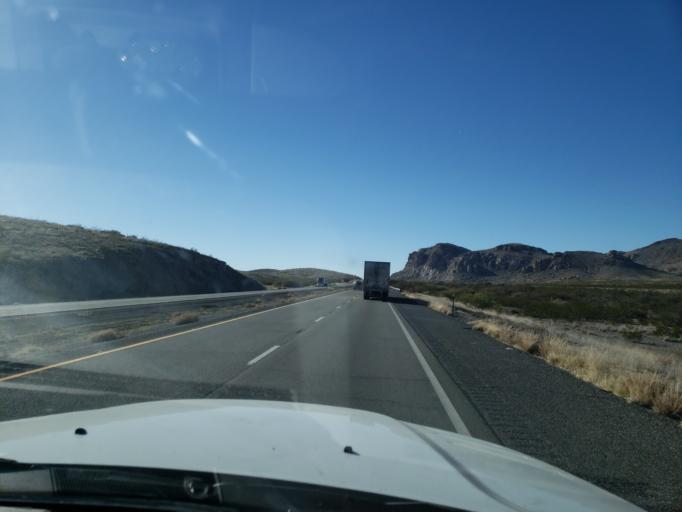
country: US
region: New Mexico
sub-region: Hidalgo County
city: Lordsburg
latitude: 32.2272
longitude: -108.9795
